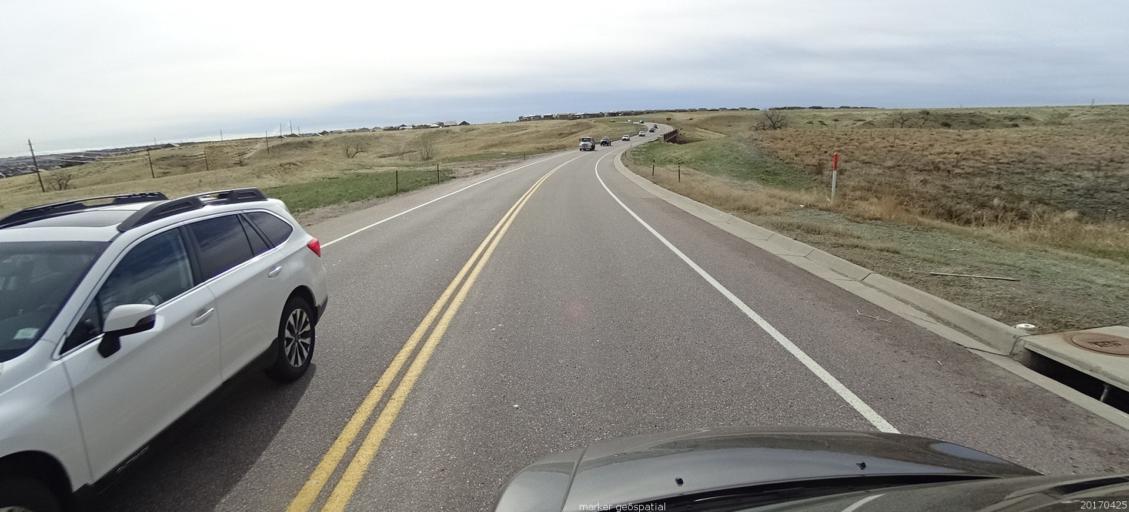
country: US
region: Colorado
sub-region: Douglas County
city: Stonegate
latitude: 39.5213
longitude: -104.8371
